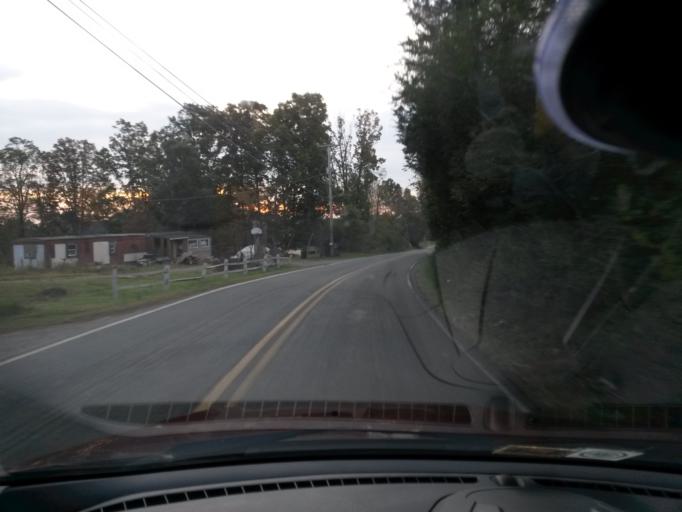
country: US
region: Virginia
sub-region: Franklin County
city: North Shore
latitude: 37.1415
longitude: -79.7793
